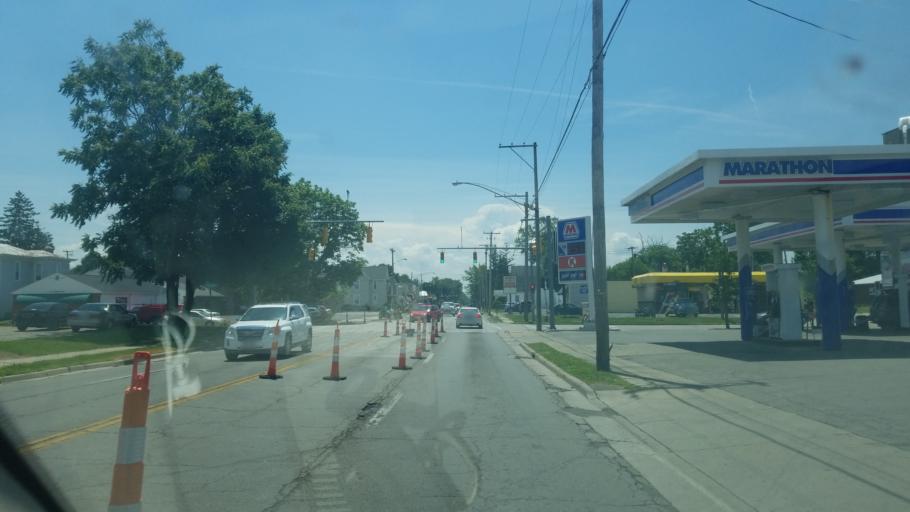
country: US
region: Ohio
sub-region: Hancock County
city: Findlay
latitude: 41.0373
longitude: -83.6413
